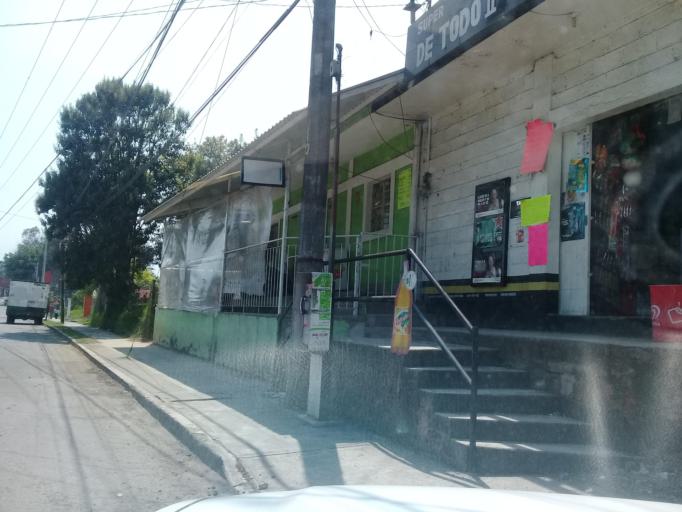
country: MX
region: Veracruz
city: Ixtac Zoquitlan
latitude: 18.8748
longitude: -97.0570
